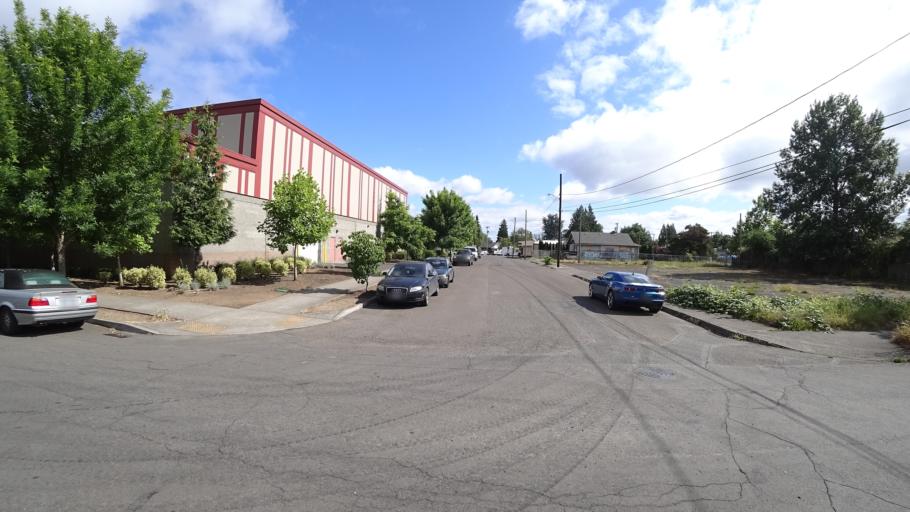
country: US
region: Oregon
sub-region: Washington County
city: West Haven
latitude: 45.5885
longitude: -122.7496
